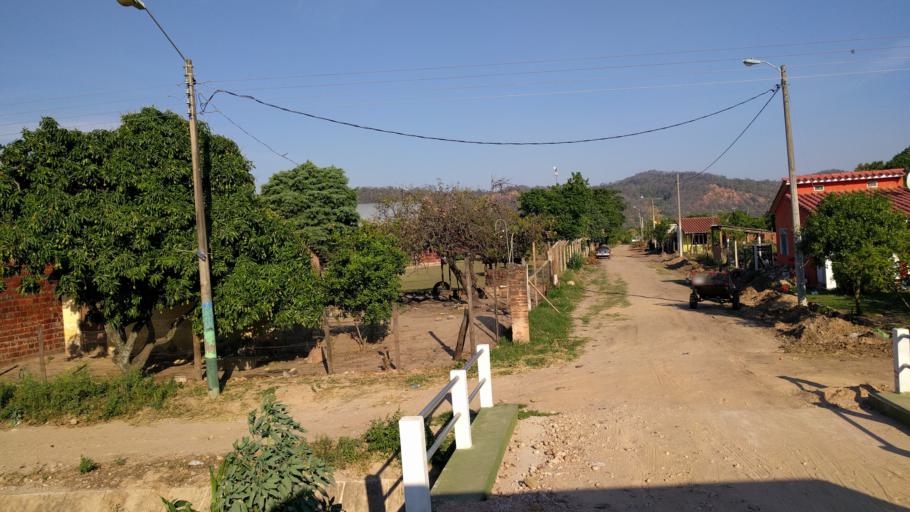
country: BO
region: Santa Cruz
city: Jorochito
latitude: -18.1180
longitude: -63.4617
